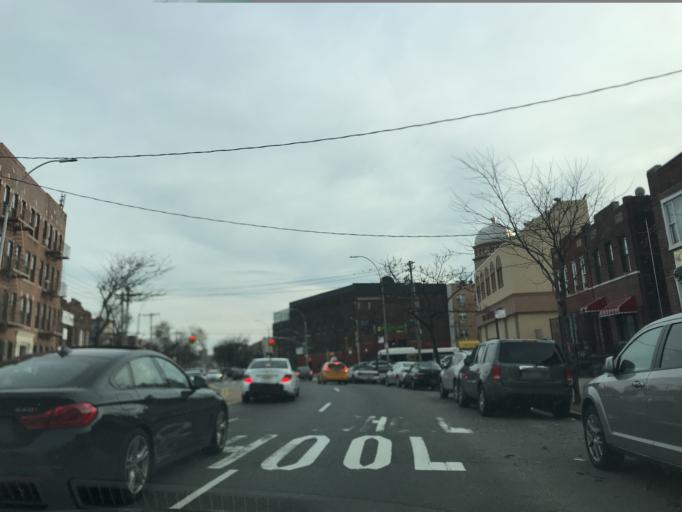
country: US
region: New York
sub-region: Kings County
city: East New York
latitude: 40.6626
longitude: -73.8935
